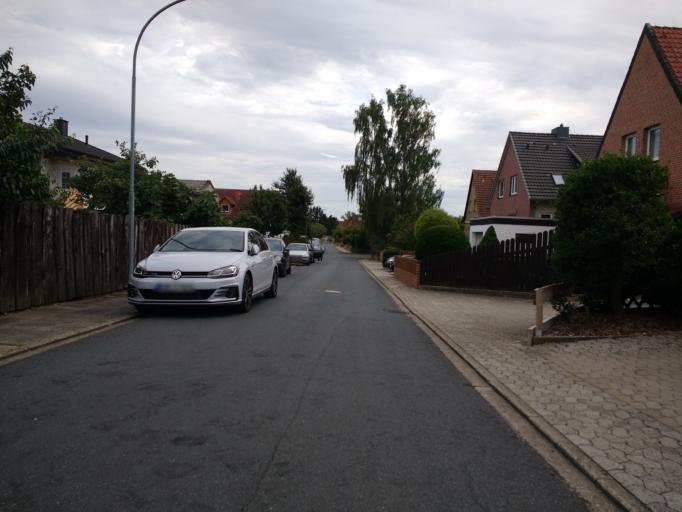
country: DE
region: Lower Saxony
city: Gifhorn
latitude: 52.5001
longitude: 10.5395
